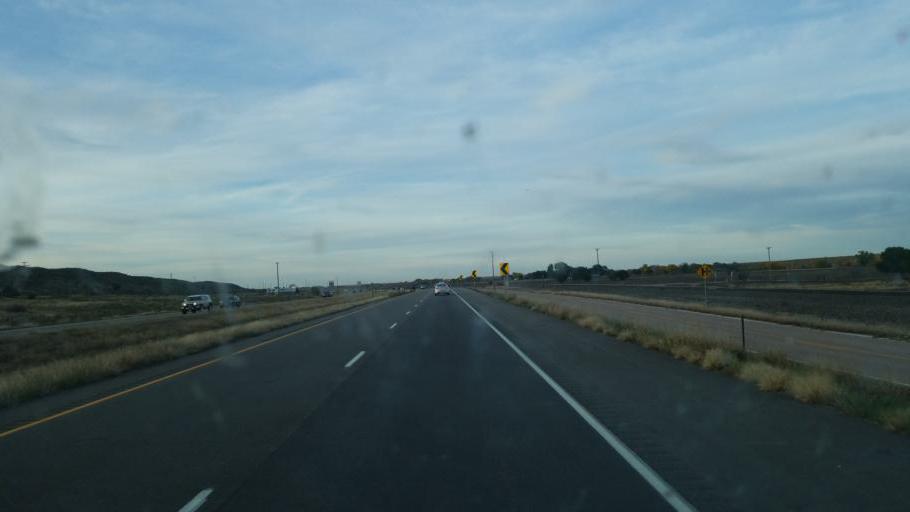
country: US
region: Colorado
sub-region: Pueblo County
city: Pueblo West
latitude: 38.4454
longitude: -104.6057
